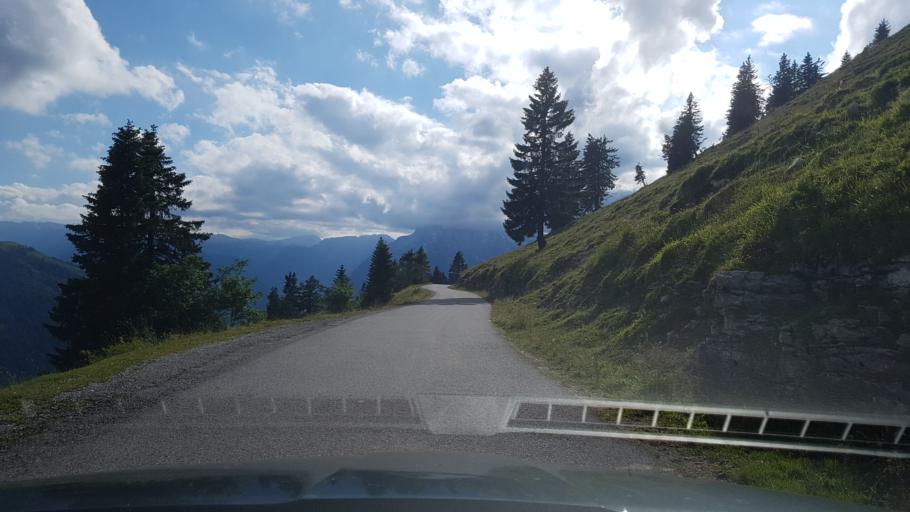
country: AT
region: Salzburg
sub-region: Politischer Bezirk Salzburg-Umgebung
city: Hintersee
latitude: 47.6363
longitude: 13.2699
